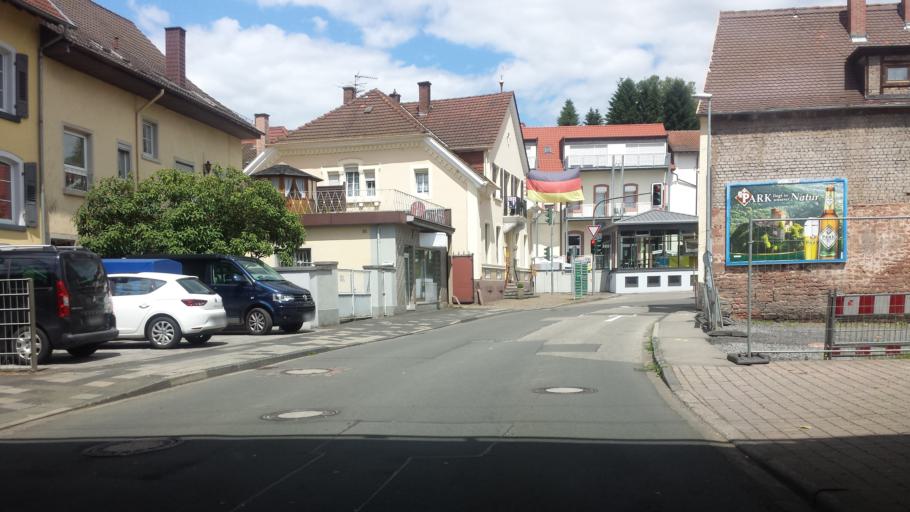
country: DE
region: Rheinland-Pfalz
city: Hochspeyer
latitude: 49.4432
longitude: 7.8958
